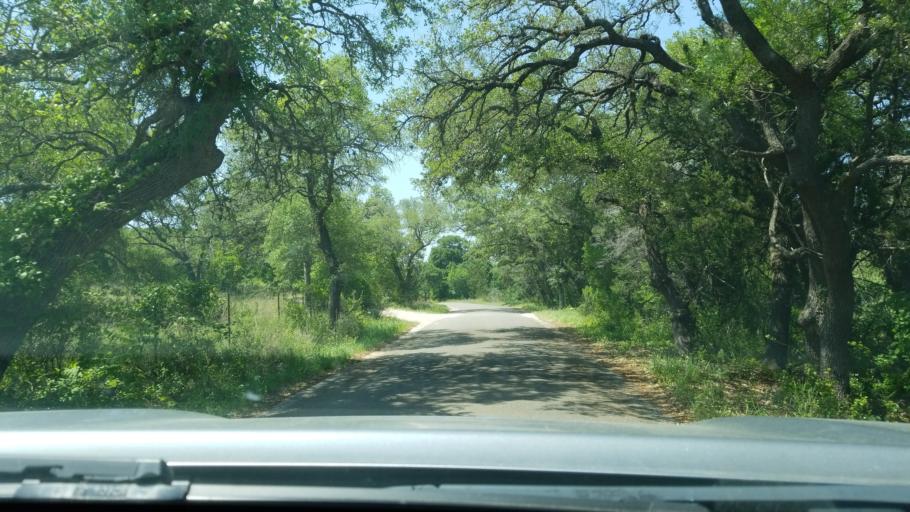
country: US
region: Texas
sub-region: Blanco County
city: Blanco
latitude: 30.0018
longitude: -98.4238
